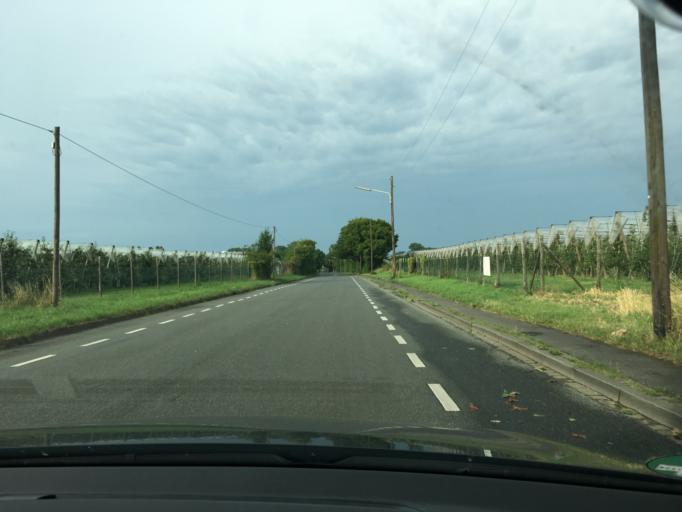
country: DE
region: North Rhine-Westphalia
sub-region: Regierungsbezirk Koln
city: Bonn
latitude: 50.7644
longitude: 7.0586
